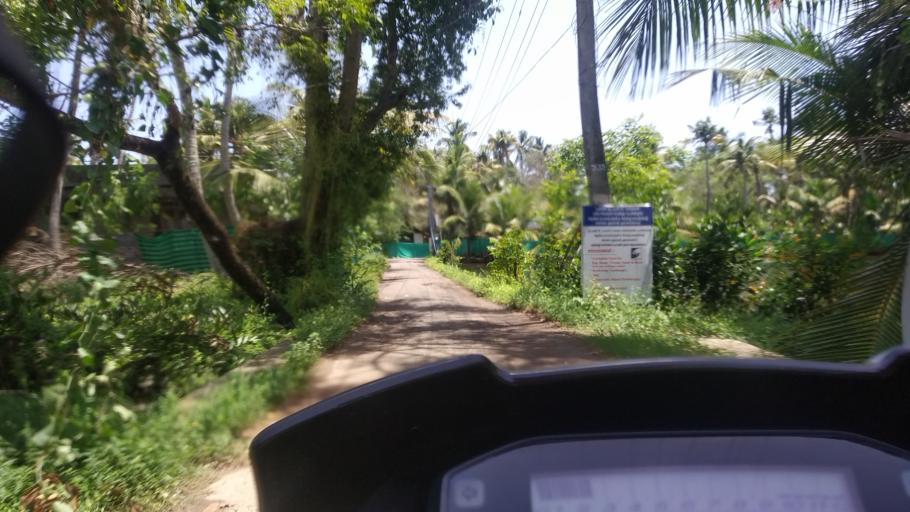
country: IN
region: Kerala
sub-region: Ernakulam
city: Elur
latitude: 10.0763
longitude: 76.2073
